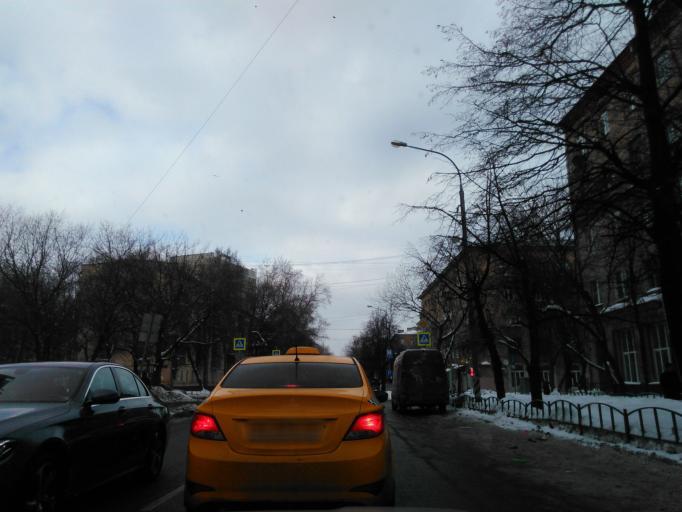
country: RU
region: Moscow
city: Sokol
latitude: 55.8010
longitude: 37.5651
